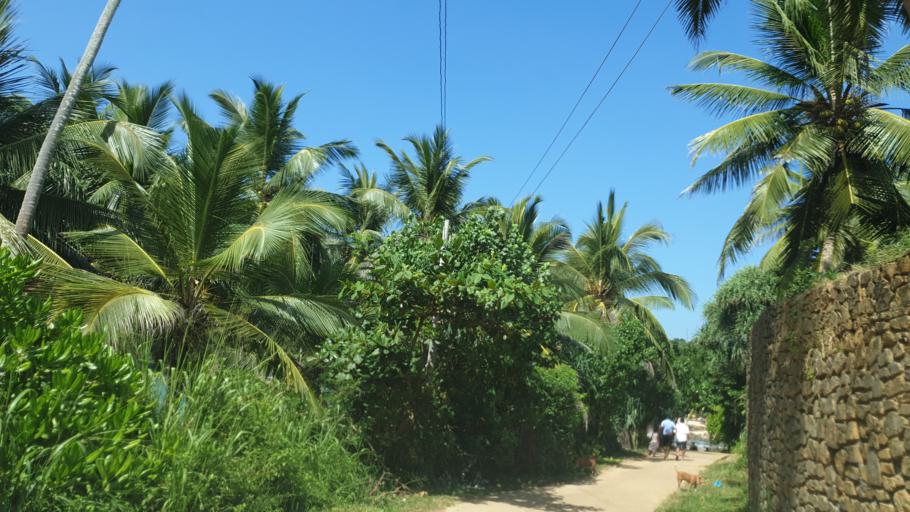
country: LK
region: Southern
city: Tangalla
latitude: 5.9613
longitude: 80.7104
